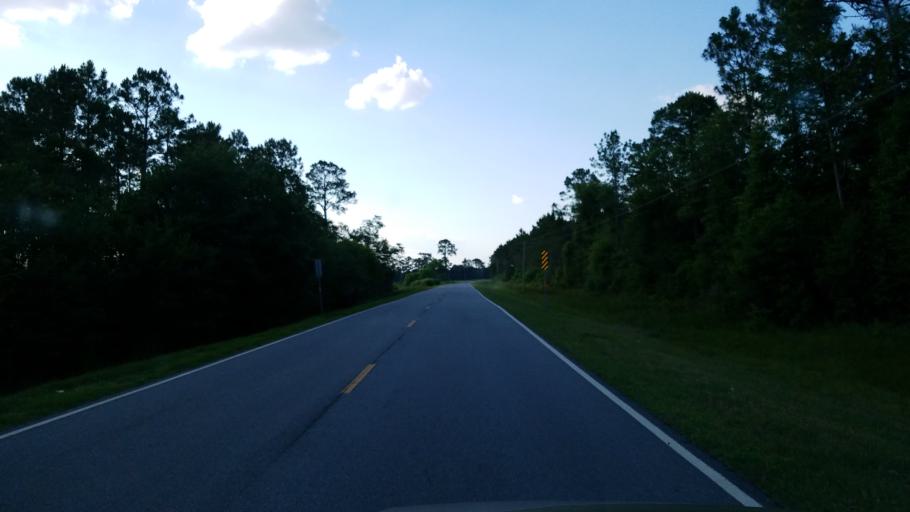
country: US
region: Georgia
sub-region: Lanier County
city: Lakeland
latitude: 31.1276
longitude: -83.0851
